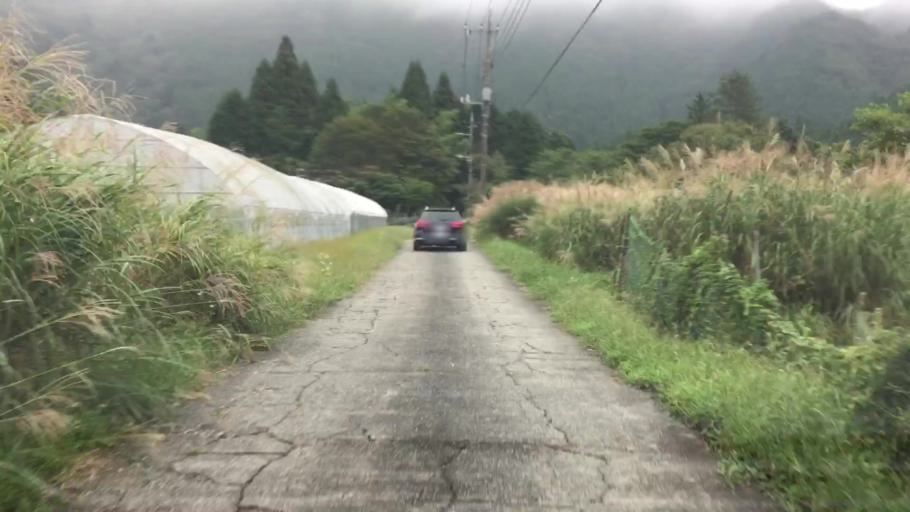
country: JP
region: Yamanashi
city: Fujikawaguchiko
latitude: 35.4041
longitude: 138.5662
